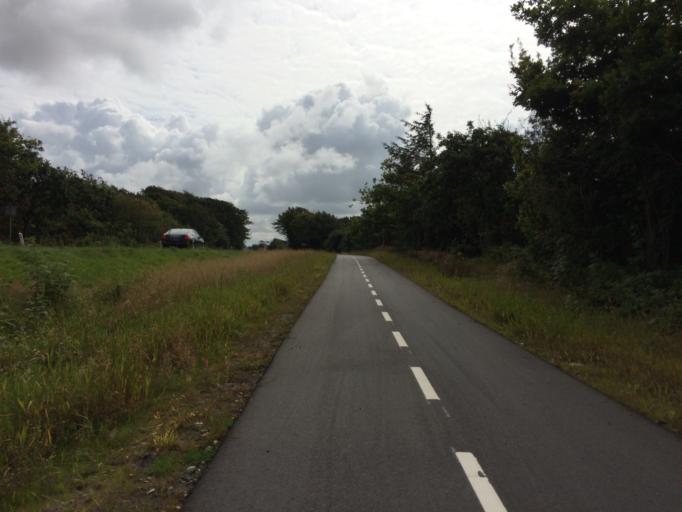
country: DK
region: Central Jutland
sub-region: Holstebro Kommune
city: Ulfborg
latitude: 56.3154
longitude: 8.3388
